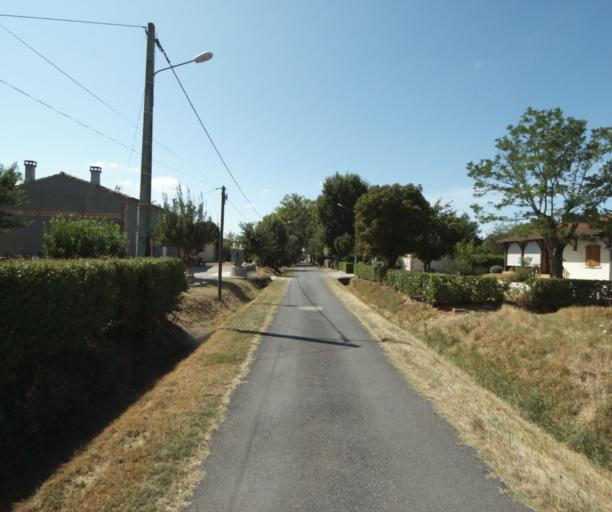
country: FR
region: Midi-Pyrenees
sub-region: Departement de la Haute-Garonne
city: Revel
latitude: 43.5000
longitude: 1.9995
